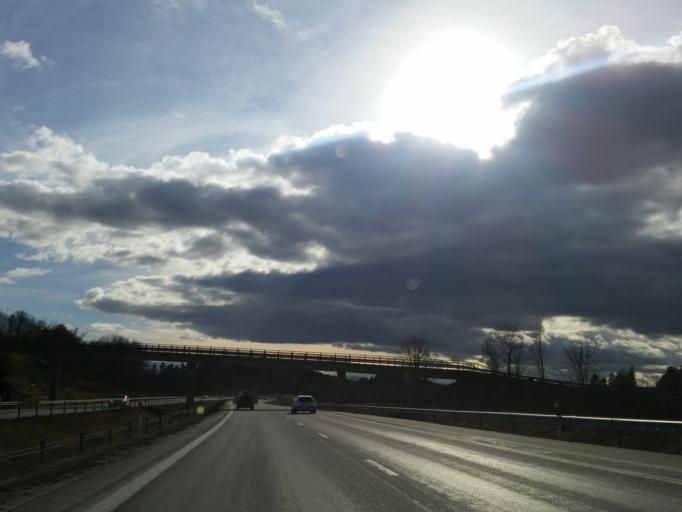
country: SE
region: Soedermanland
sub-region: Gnesta Kommun
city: Gnesta
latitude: 58.8905
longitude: 17.2637
